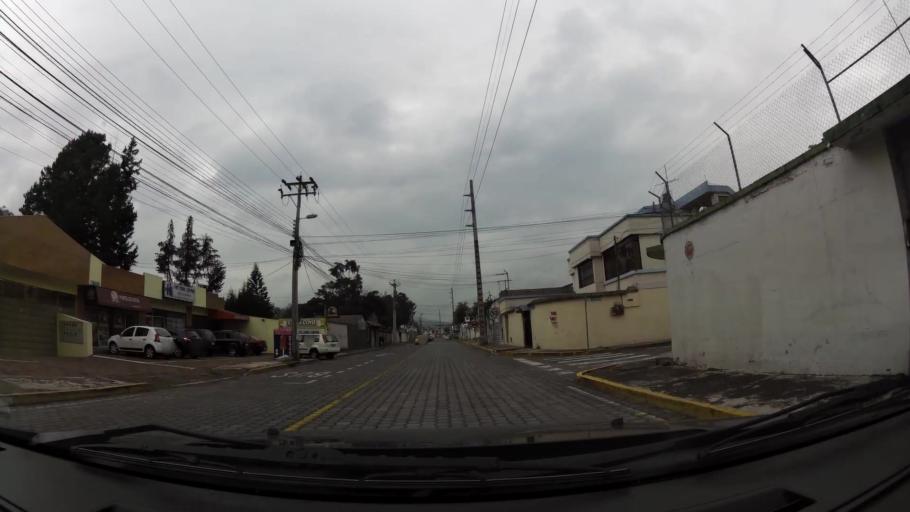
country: EC
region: Pichincha
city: Sangolqui
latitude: -0.3161
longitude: -78.4586
